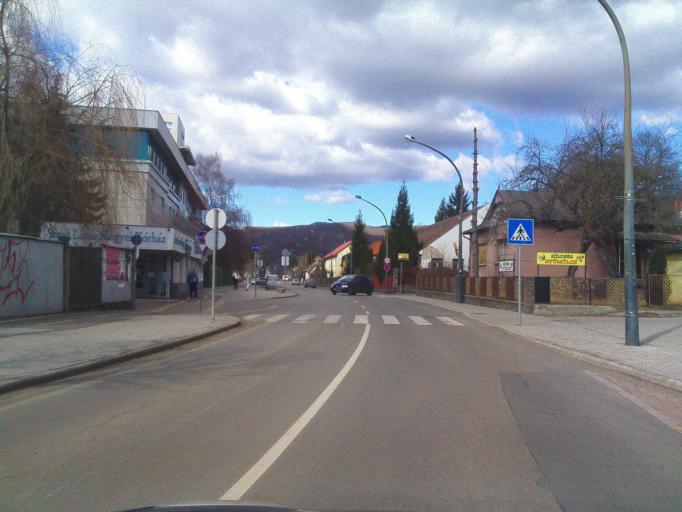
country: HU
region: Nograd
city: Salgotarjan
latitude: 48.1145
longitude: 19.8112
